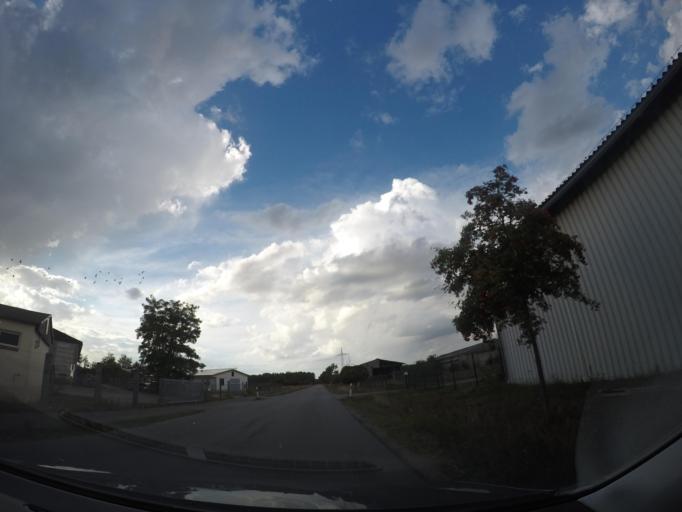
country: DE
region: Saxony-Anhalt
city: Calvorde
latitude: 52.4469
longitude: 11.3024
